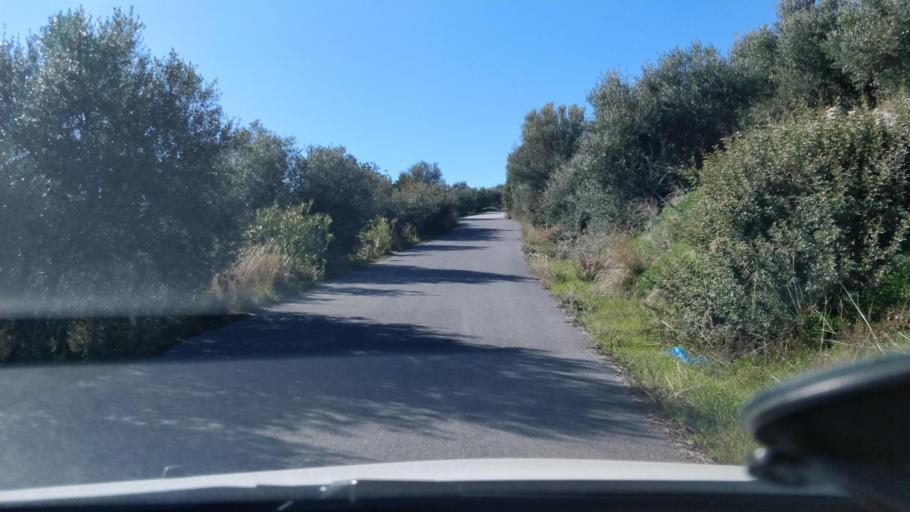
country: GR
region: Crete
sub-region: Nomos Lasithiou
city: Gra Liyia
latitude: 35.0196
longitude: 25.5537
